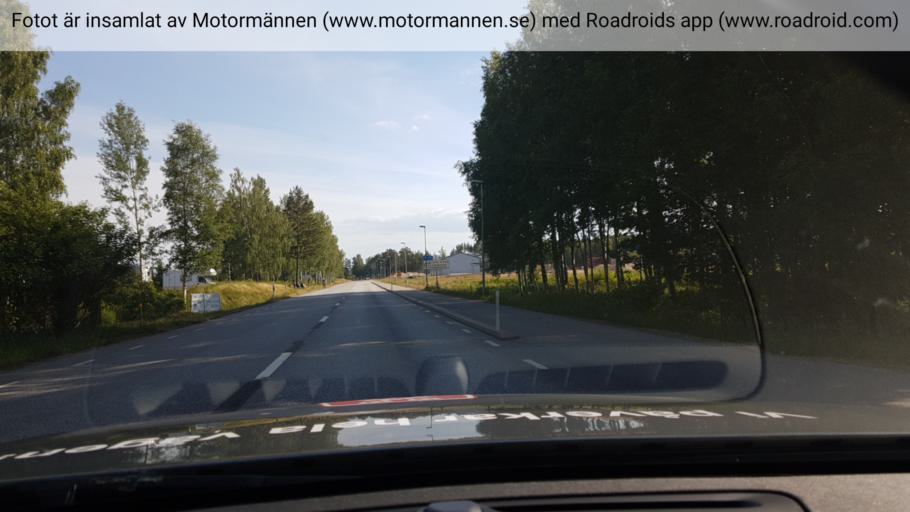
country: SE
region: Vaestra Goetaland
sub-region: Karlsborgs Kommun
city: Karlsborg
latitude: 58.5543
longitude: 14.5010
